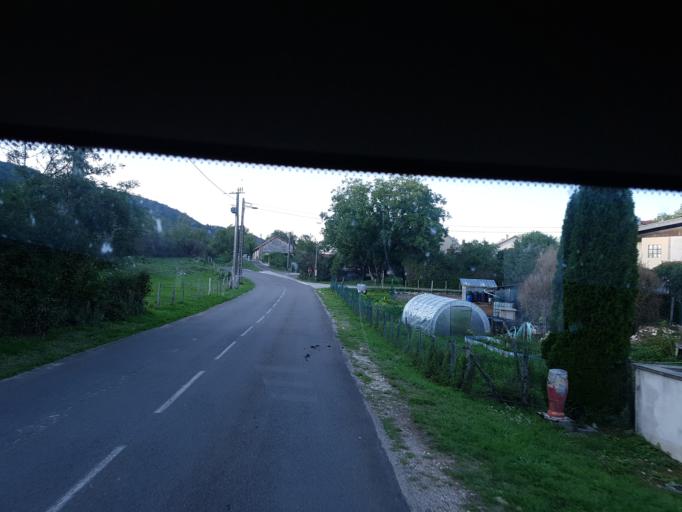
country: FR
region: Franche-Comte
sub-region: Departement du Jura
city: Moirans-en-Montagne
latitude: 46.4048
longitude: 5.6486
